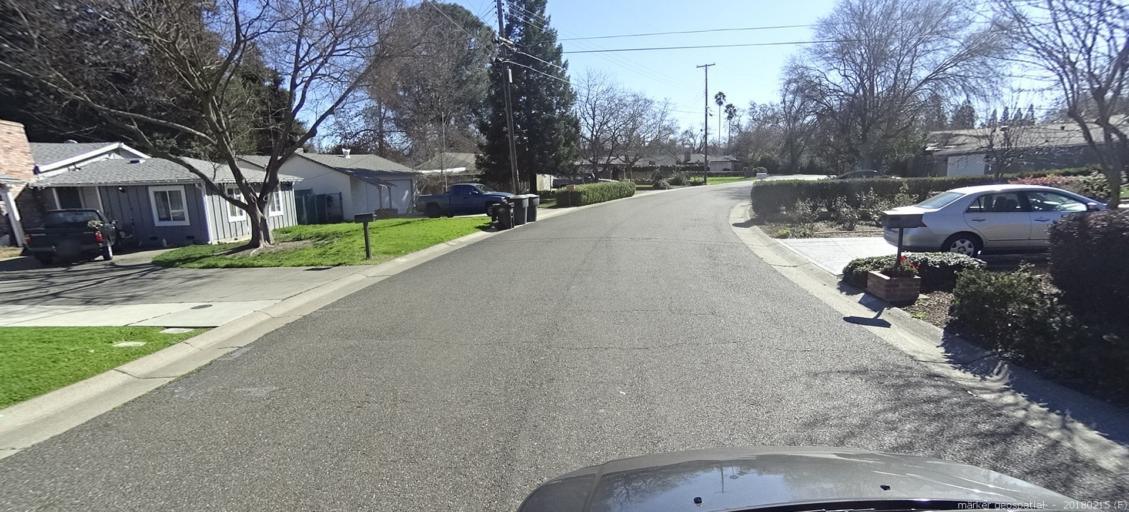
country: US
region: California
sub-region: Sacramento County
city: Fair Oaks
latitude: 38.6672
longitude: -121.3058
